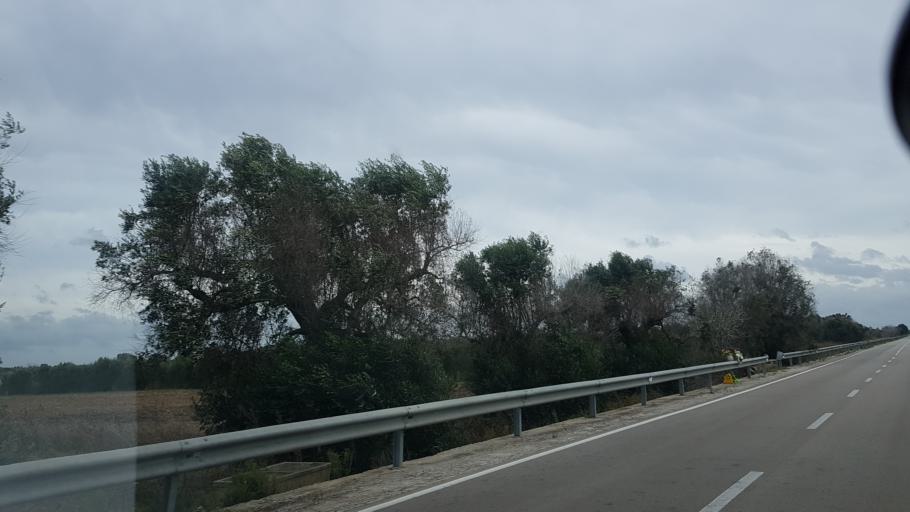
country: IT
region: Apulia
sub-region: Provincia di Brindisi
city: San Donaci
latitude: 40.4044
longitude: 17.8970
